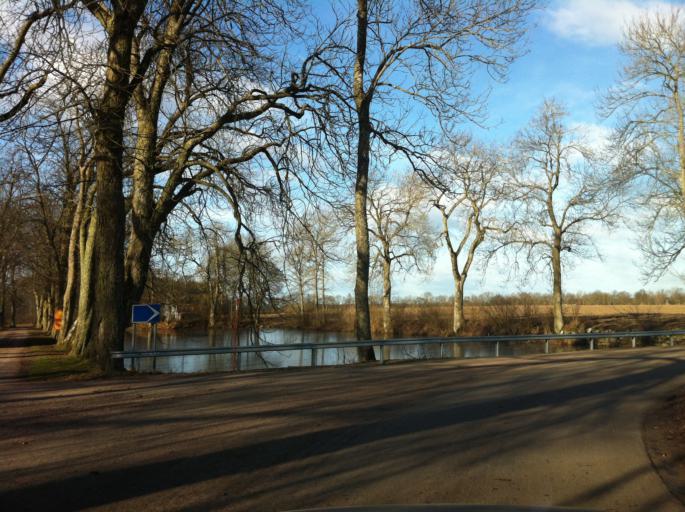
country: SE
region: Skane
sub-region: Landskrona
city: Asmundtorp
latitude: 55.9534
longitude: 12.9335
